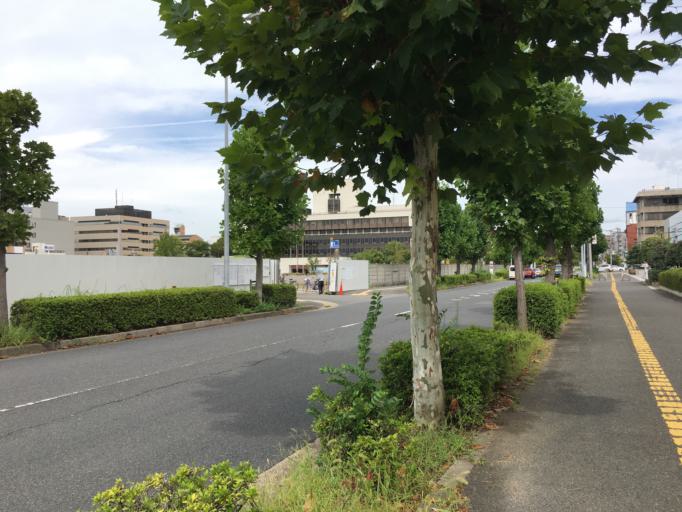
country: JP
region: Nara
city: Nara-shi
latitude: 34.6831
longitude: 135.8058
